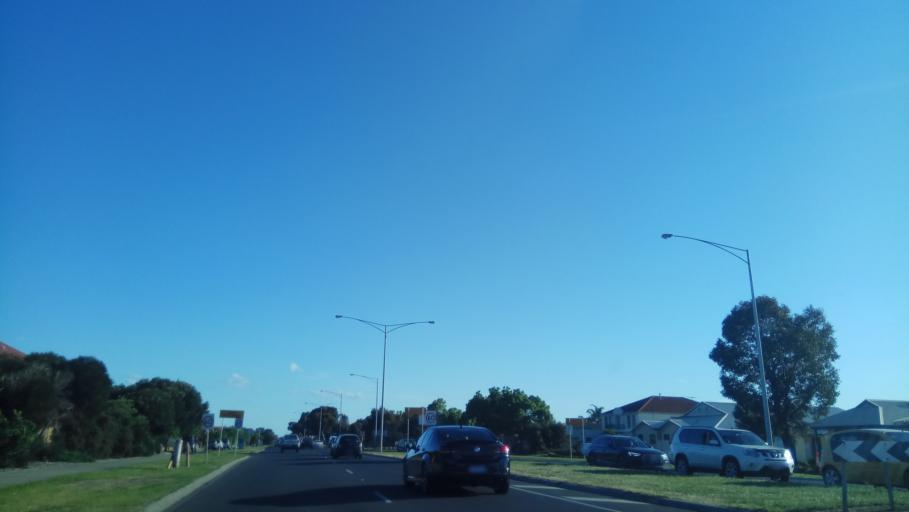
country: AU
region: Victoria
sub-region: Hobsons Bay
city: Altona Meadows
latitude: -37.8874
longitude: 144.7560
